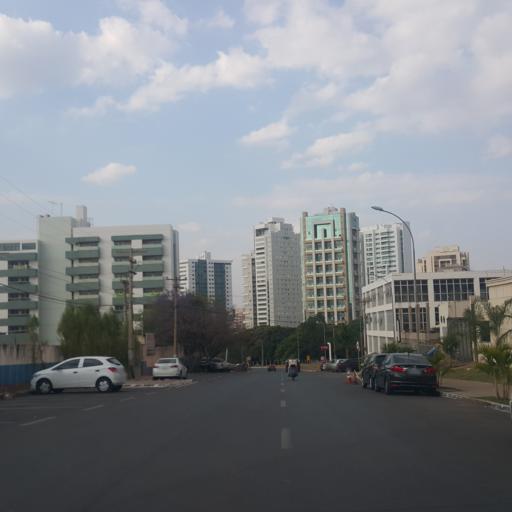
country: BR
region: Federal District
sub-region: Brasilia
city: Brasilia
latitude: -15.8466
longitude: -48.0322
